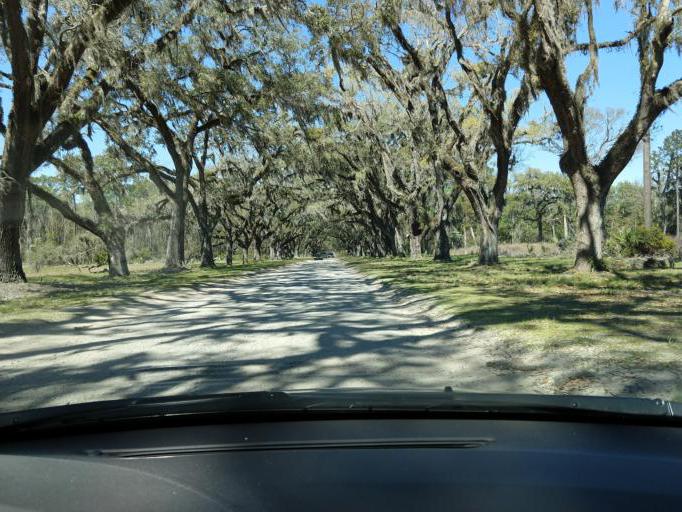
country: US
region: Georgia
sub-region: Chatham County
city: Isle of Hope
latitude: 31.9702
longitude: -81.0692
